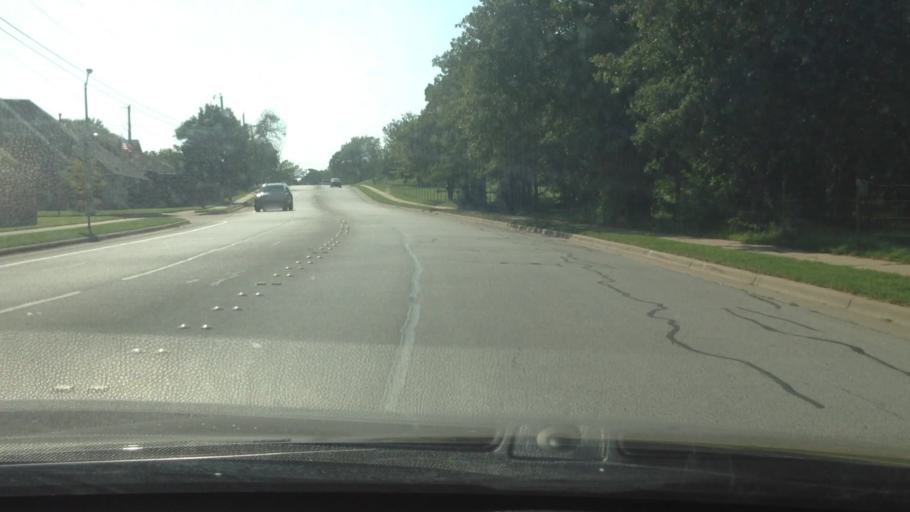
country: US
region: Texas
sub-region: Tarrant County
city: Colleyville
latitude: 32.8839
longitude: -97.1897
